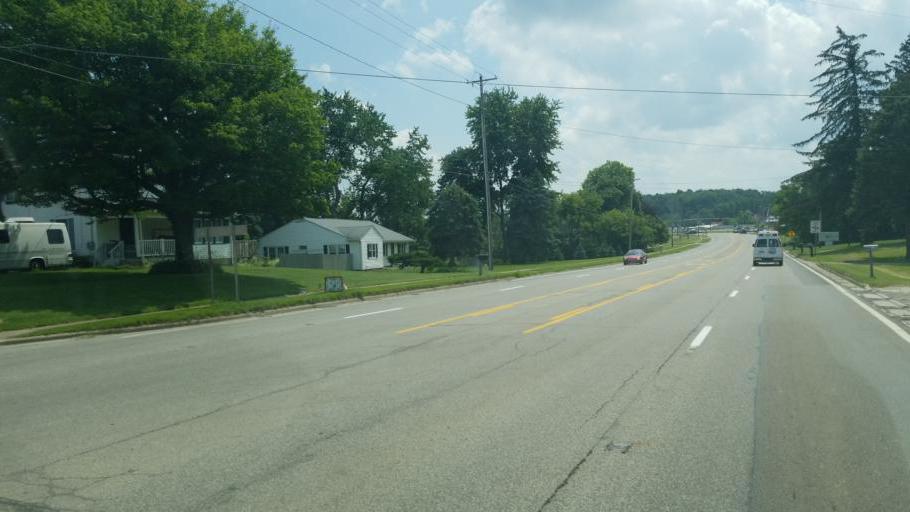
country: US
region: Ohio
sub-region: Richland County
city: Ontario
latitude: 40.7863
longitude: -82.5551
